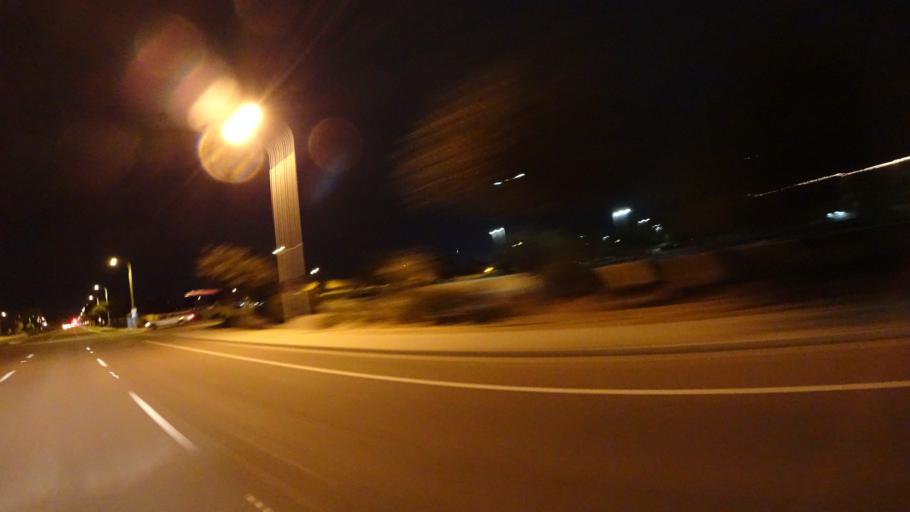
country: US
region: Arizona
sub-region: Maricopa County
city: Chandler
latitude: 33.3064
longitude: -111.8039
